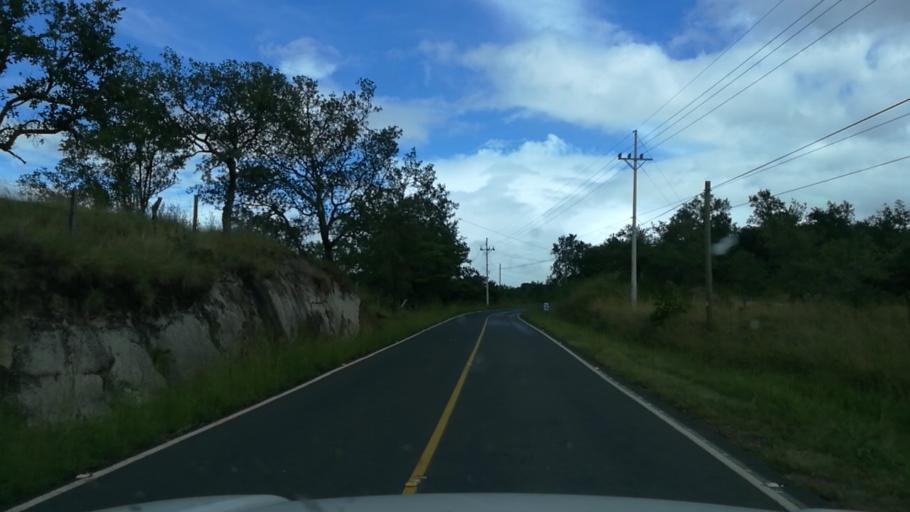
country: CR
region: Guanacaste
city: Fortuna
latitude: 10.6287
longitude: -85.2318
